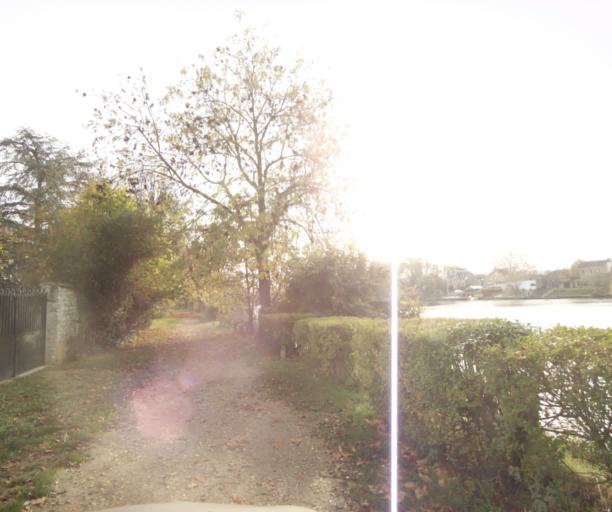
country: FR
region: Ile-de-France
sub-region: Departement des Yvelines
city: Triel-sur-Seine
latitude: 48.9833
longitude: 1.9995
